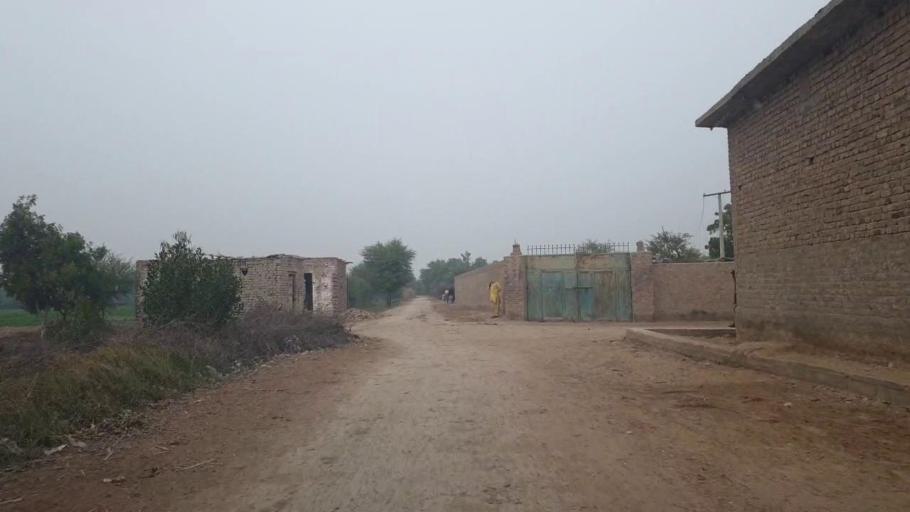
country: PK
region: Sindh
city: Tando Adam
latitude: 25.7792
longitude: 68.6985
